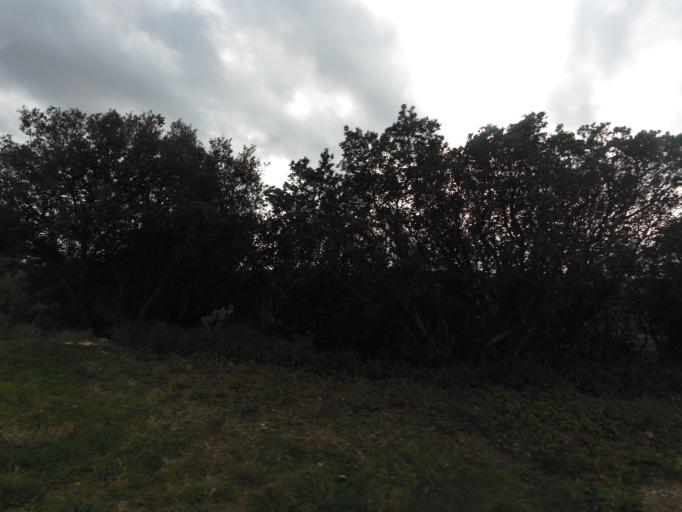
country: FR
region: Languedoc-Roussillon
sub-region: Departement du Gard
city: Clarensac
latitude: 43.8354
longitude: 4.1877
